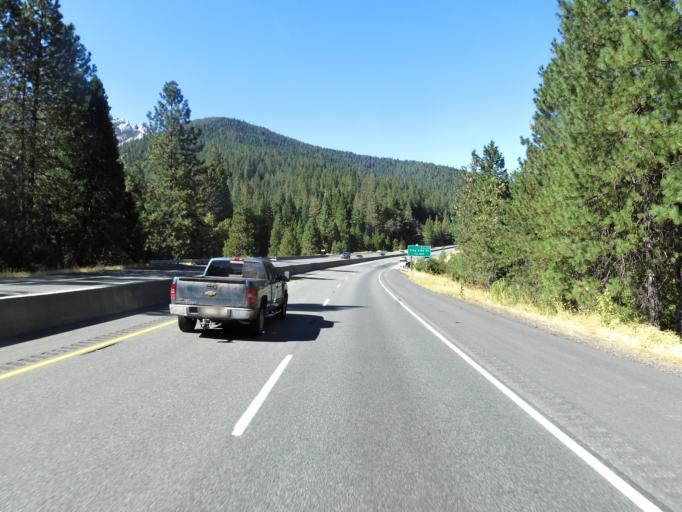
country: US
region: California
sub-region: Siskiyou County
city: Dunsmuir
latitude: 41.1616
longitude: -122.2969
